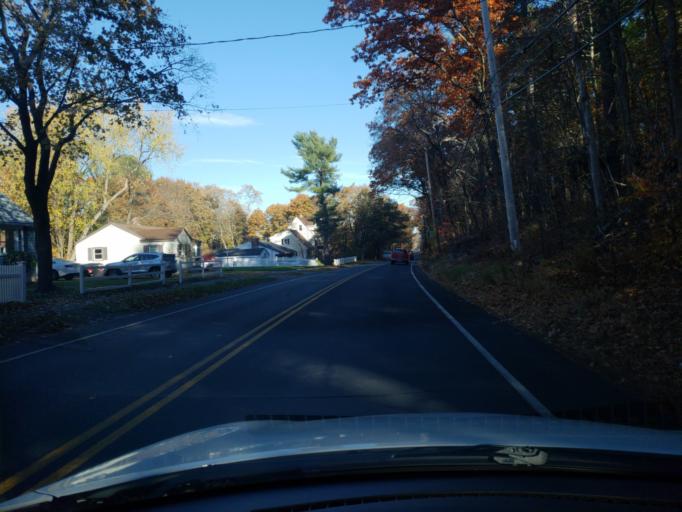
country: US
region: Massachusetts
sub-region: Essex County
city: Andover
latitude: 42.6664
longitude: -71.1404
